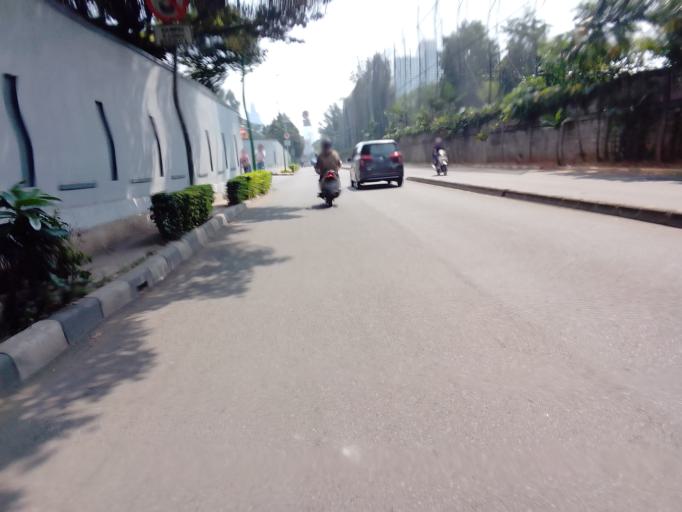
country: ID
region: Jakarta Raya
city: Jakarta
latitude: -6.2215
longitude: 106.7949
